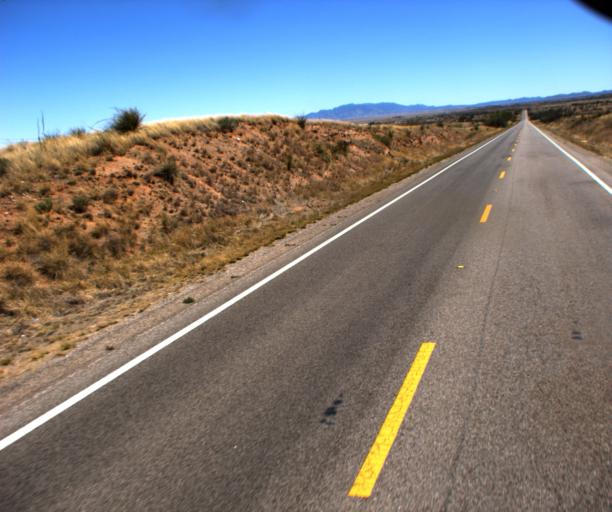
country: US
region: Arizona
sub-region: Pima County
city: Corona de Tucson
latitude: 31.7617
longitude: -110.6783
